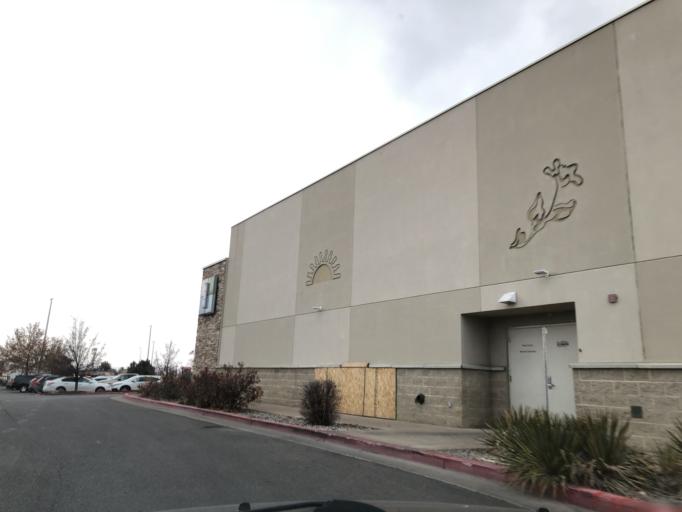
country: US
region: Utah
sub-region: Cache County
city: Logan
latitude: 41.7555
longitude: -111.8319
